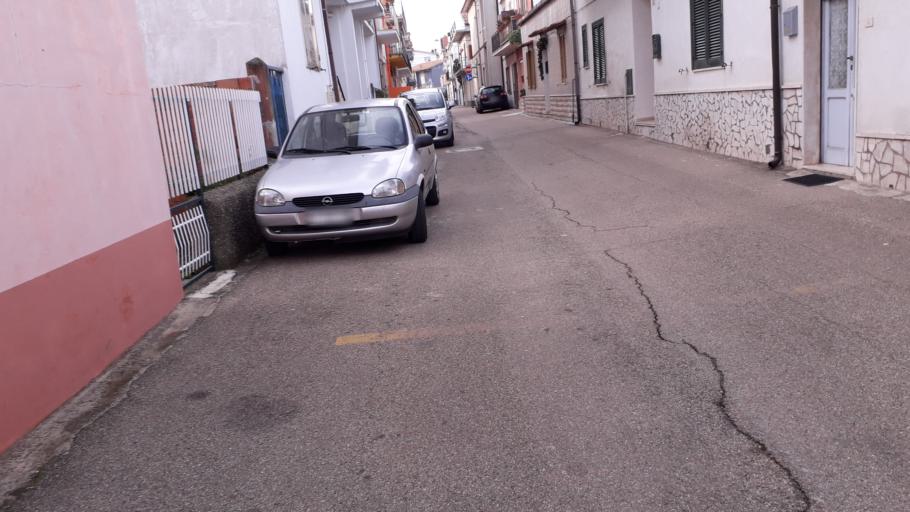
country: IT
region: Molise
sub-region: Provincia di Campobasso
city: Campomarino
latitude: 41.9556
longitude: 15.0331
